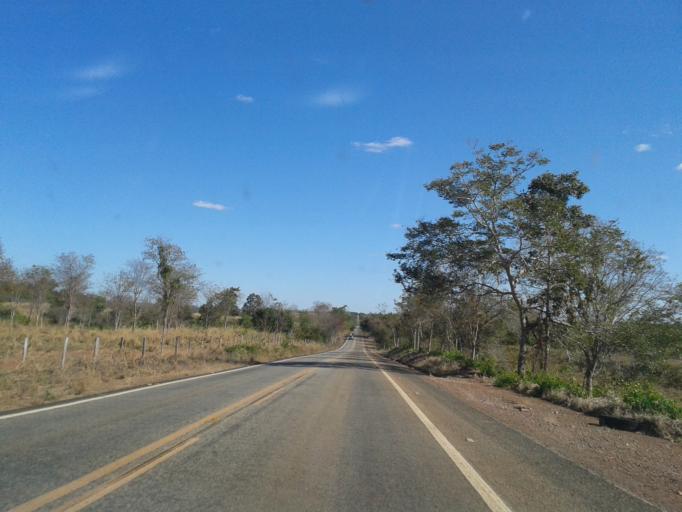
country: BR
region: Goias
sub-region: Mozarlandia
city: Mozarlandia
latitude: -14.5650
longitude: -50.4987
